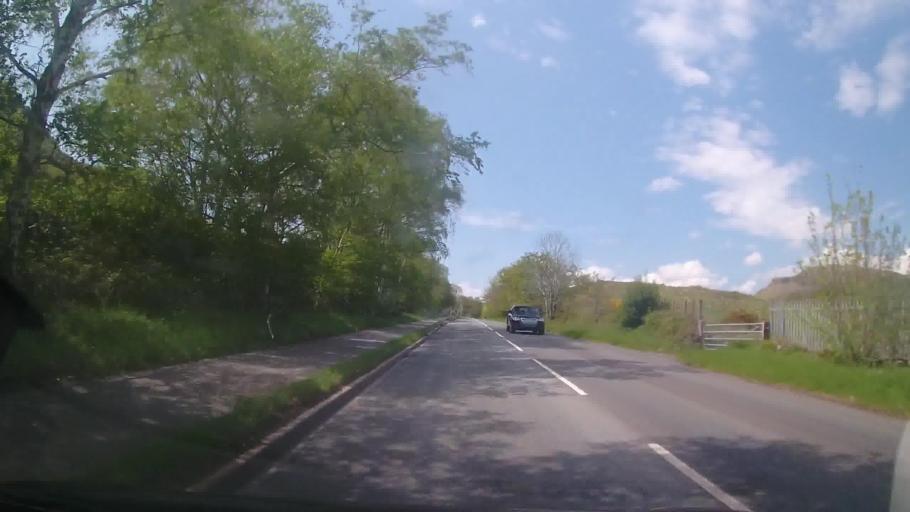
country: GB
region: Wales
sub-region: Gwynedd
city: Porthmadog
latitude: 52.9327
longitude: -4.1500
